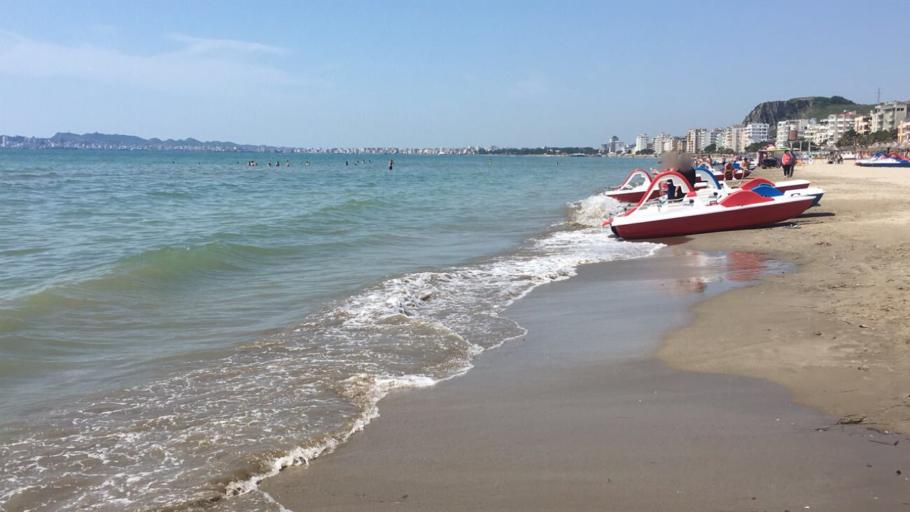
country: AL
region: Tirane
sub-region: Rrethi i Kavajes
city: Golem
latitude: 41.2661
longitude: 19.5204
